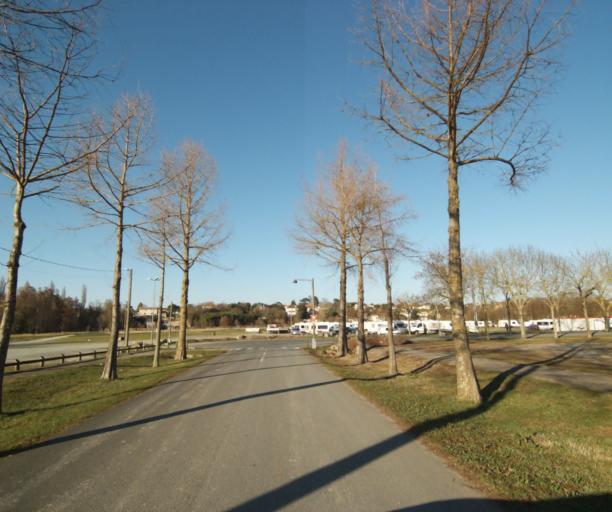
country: FR
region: Poitou-Charentes
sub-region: Departement des Deux-Sevres
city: Niort
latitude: 46.3327
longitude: -0.4900
